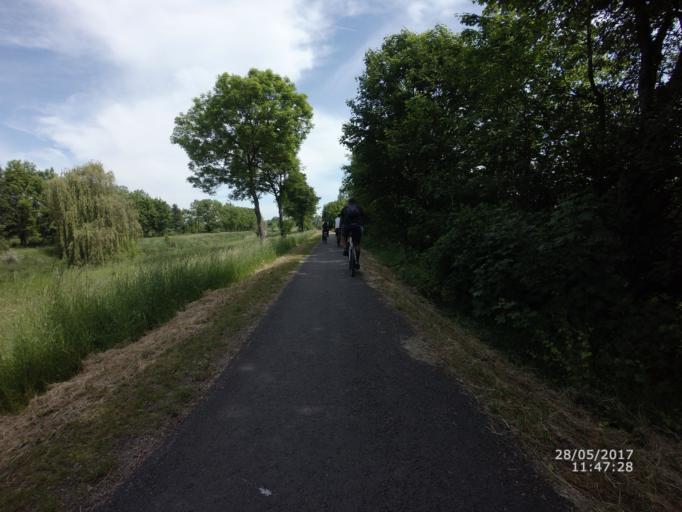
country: DE
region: Thuringia
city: Griefstedt
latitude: 51.2000
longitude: 11.1385
